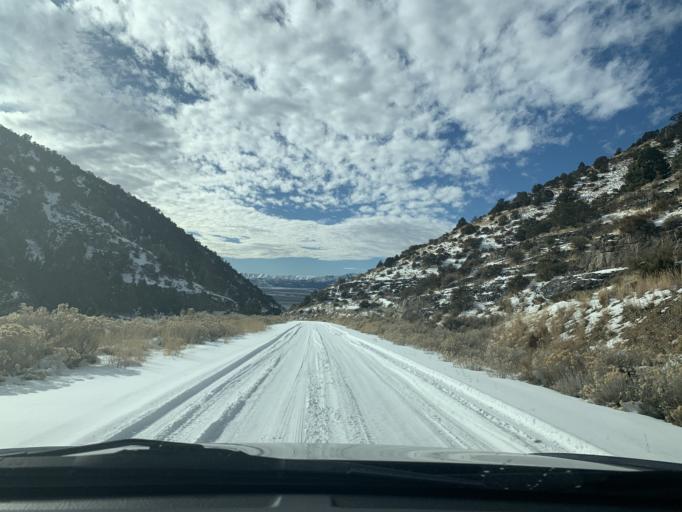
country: US
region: Utah
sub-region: Tooele County
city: Tooele
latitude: 40.3139
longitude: -112.2378
